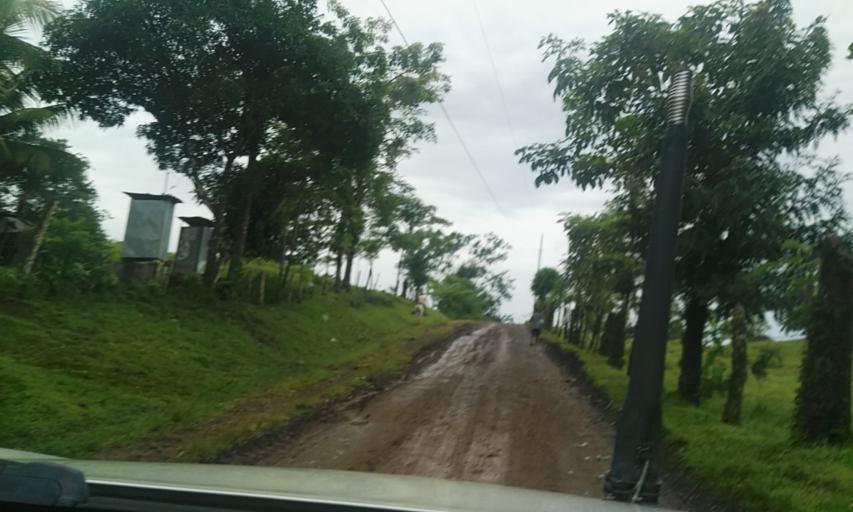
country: NI
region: Matagalpa
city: Rio Blanco
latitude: 12.9544
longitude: -85.1786
